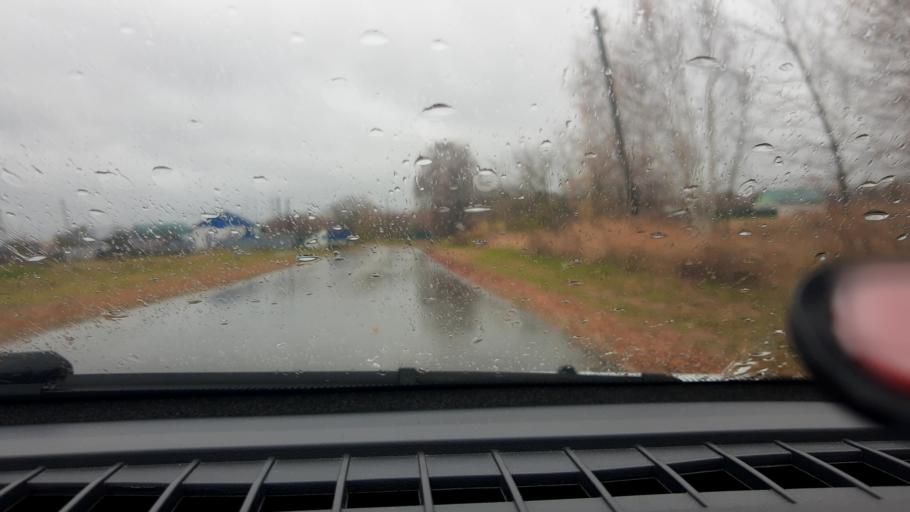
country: RU
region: Nizjnij Novgorod
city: Kstovo
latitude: 56.0744
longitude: 44.1493
